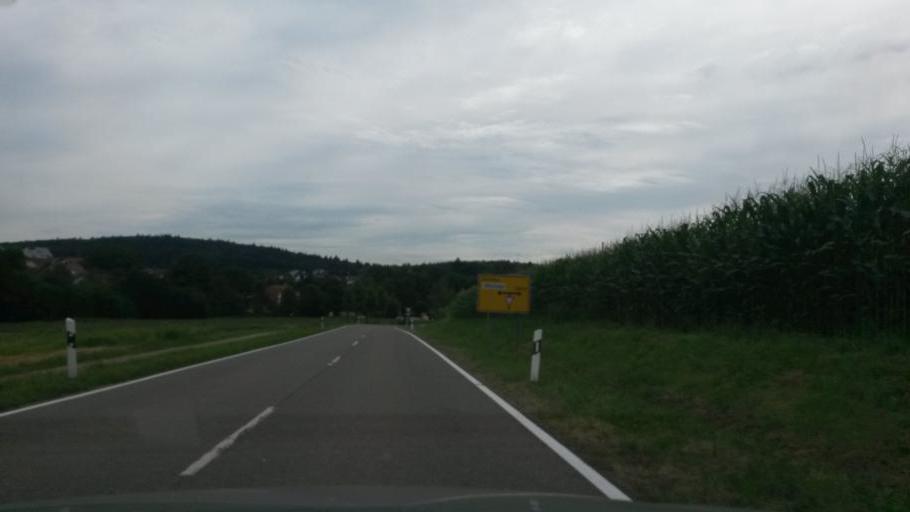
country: DE
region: Baden-Wuerttemberg
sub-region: Karlsruhe Region
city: Konigsbach-Stein
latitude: 48.9254
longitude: 8.5623
